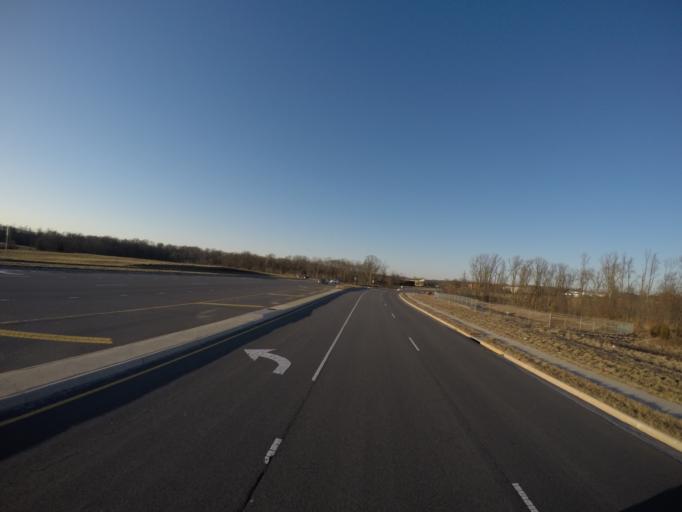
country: US
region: Virginia
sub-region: Loudoun County
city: Sterling
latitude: 39.0169
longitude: -77.4369
